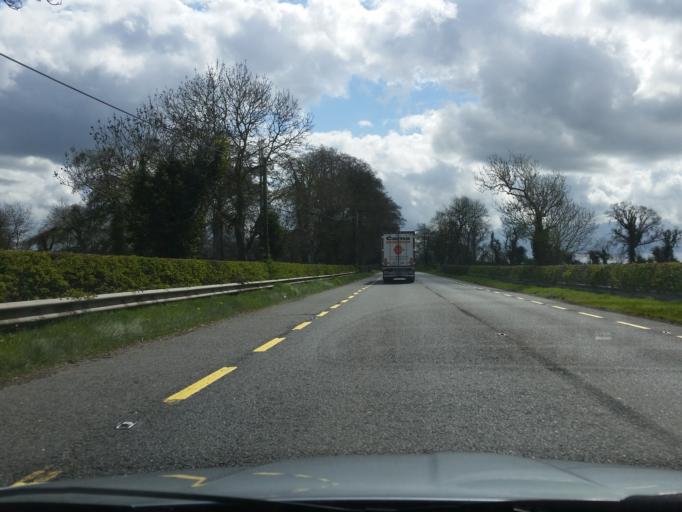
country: IE
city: Kentstown
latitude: 53.5991
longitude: -6.4692
